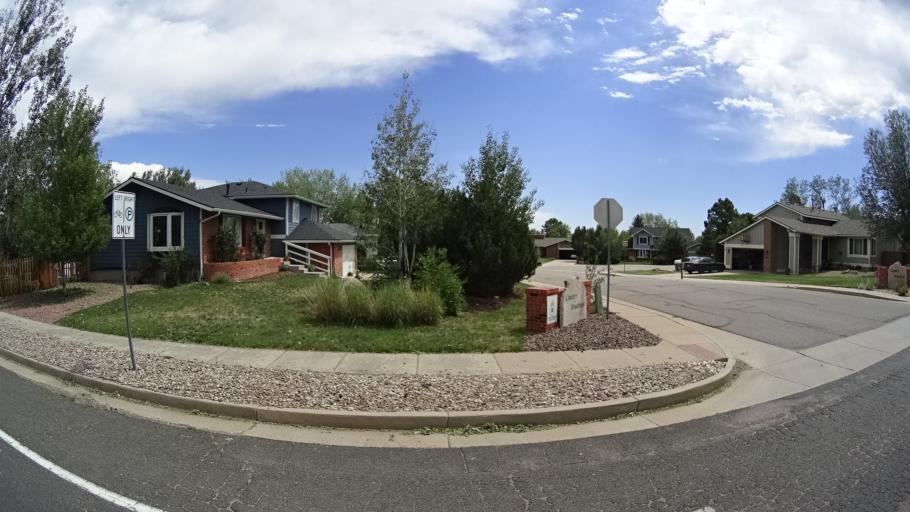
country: US
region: Colorado
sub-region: El Paso County
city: Stratmoor
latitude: 38.7719
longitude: -104.8201
